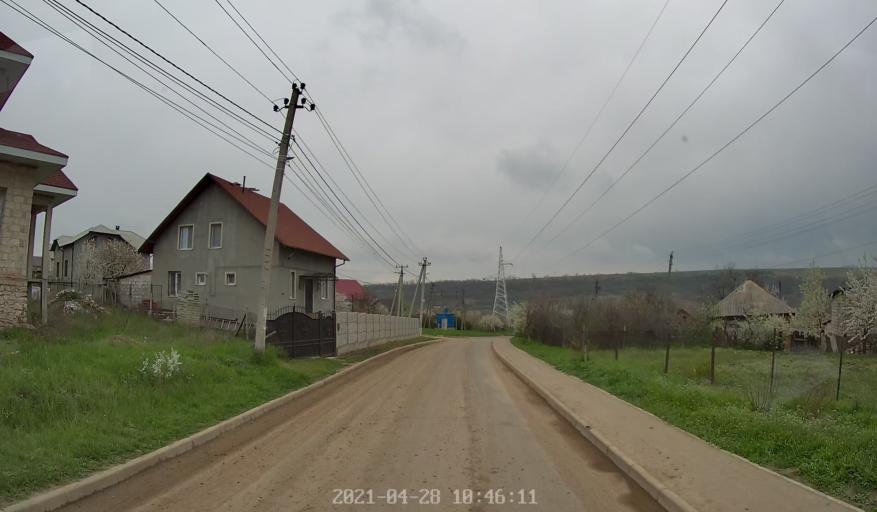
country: MD
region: Chisinau
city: Singera
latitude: 46.9899
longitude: 28.9429
